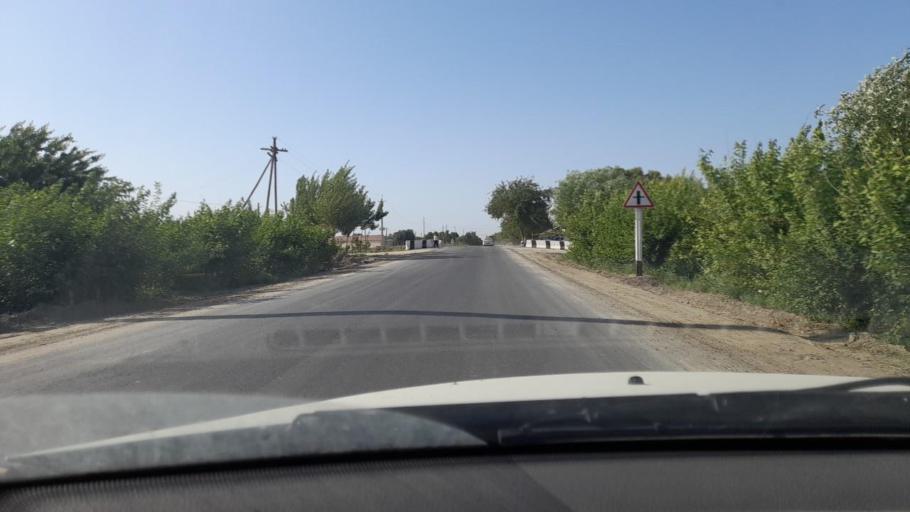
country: UZ
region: Bukhara
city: Romiton
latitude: 40.0651
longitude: 64.3271
